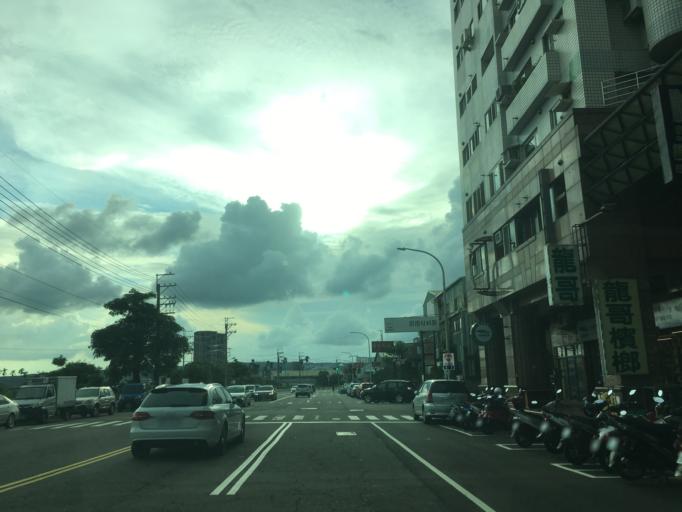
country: TW
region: Taiwan
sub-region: Taichung City
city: Taichung
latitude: 24.1359
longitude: 120.6360
